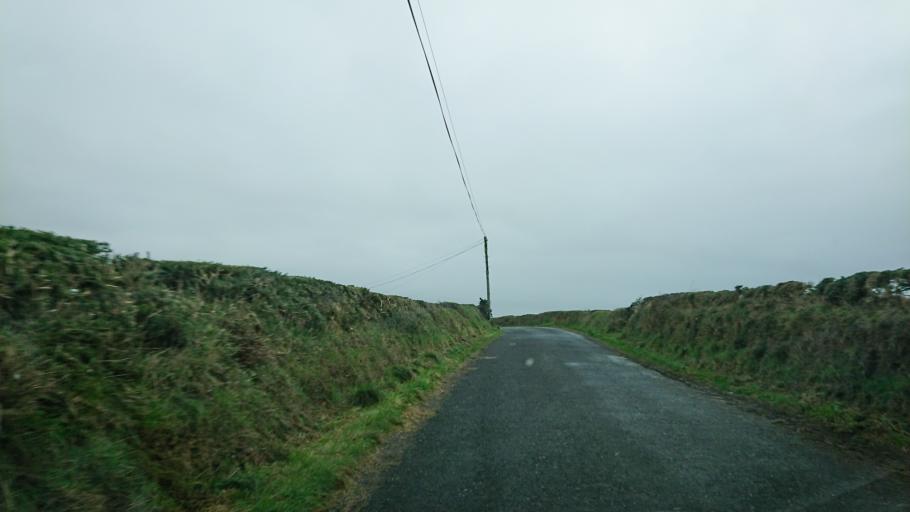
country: IE
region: Munster
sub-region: Waterford
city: Tra Mhor
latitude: 52.1432
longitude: -7.2042
